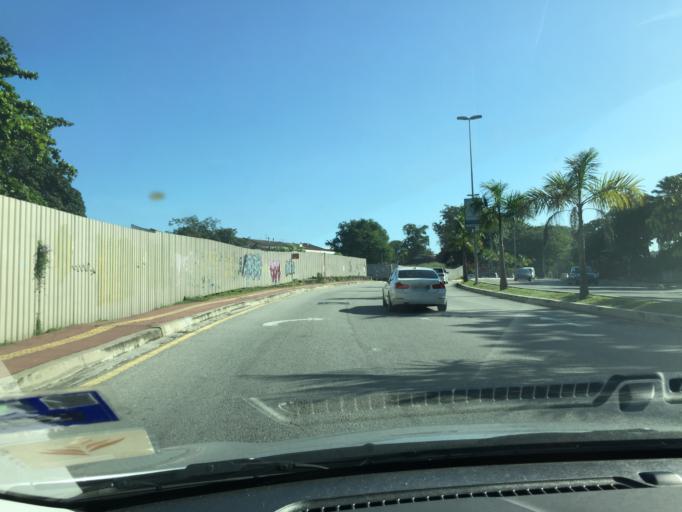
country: MY
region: Selangor
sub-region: Petaling
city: Petaling Jaya
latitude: 3.1180
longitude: 101.6304
